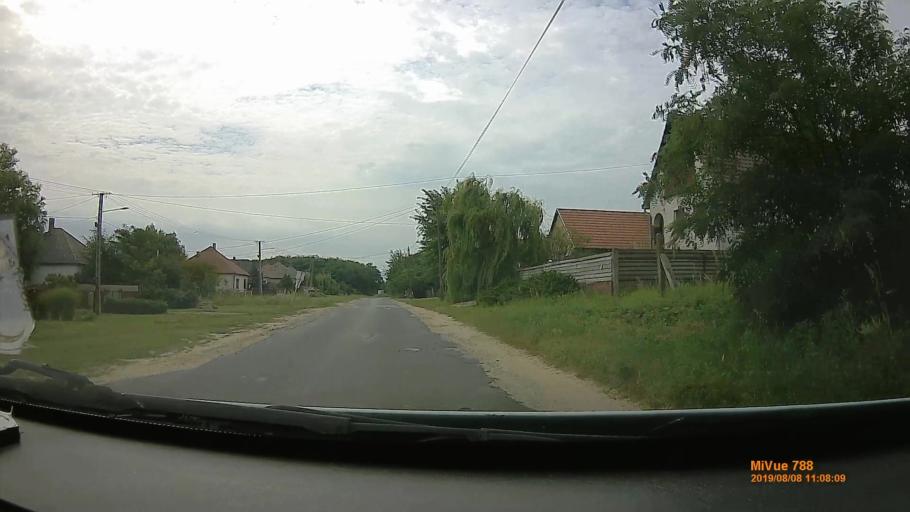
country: HU
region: Szabolcs-Szatmar-Bereg
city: Balkany
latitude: 47.7607
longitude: 21.8483
